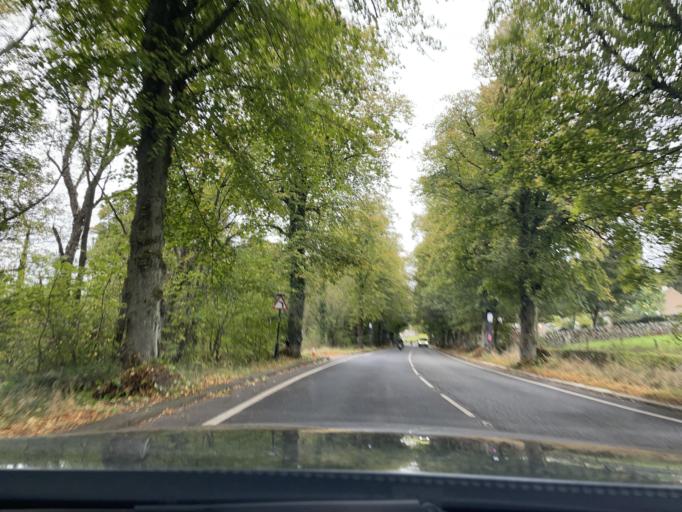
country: GB
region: England
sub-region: Sheffield
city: Oughtibridge
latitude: 53.3840
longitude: -1.5458
